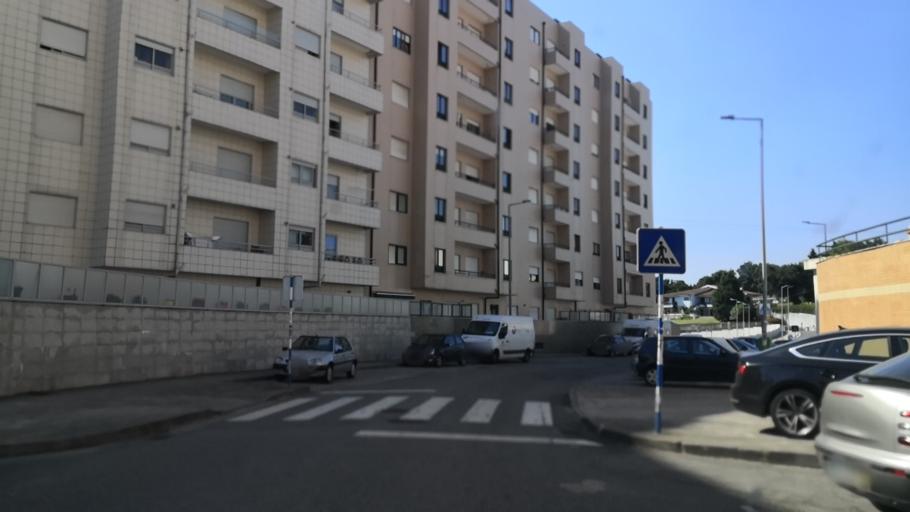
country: PT
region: Porto
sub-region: Gondomar
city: Rio Tinto
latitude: 41.1750
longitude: -8.5432
